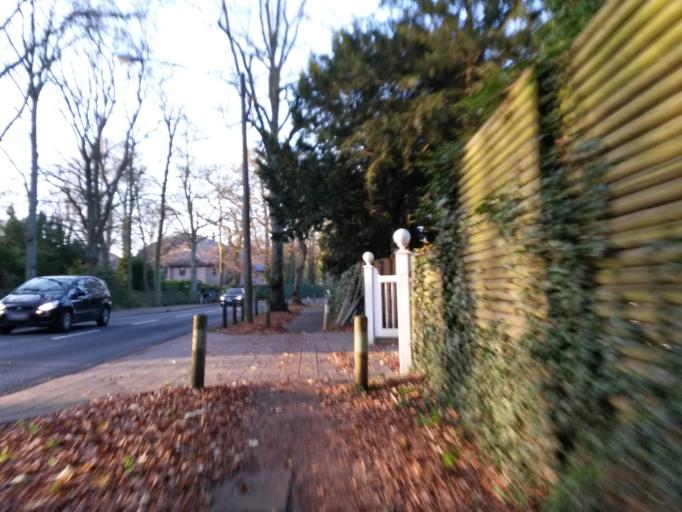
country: DE
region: Lower Saxony
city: Lilienthal
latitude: 53.0830
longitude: 8.9359
